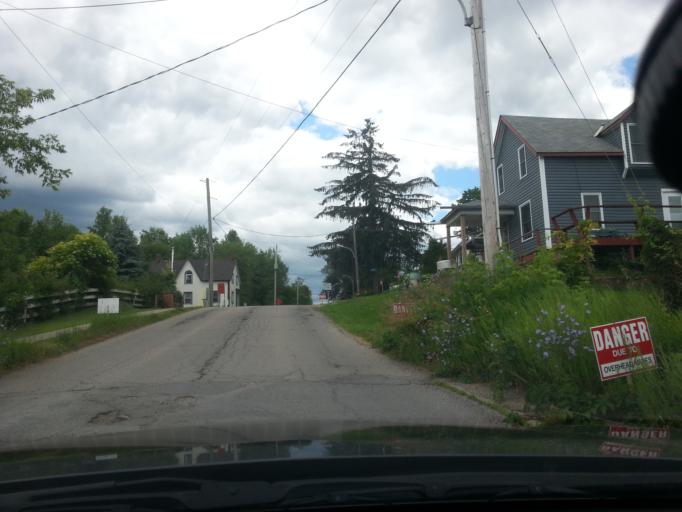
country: CA
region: Ontario
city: Gananoque
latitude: 44.6062
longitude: -76.2239
